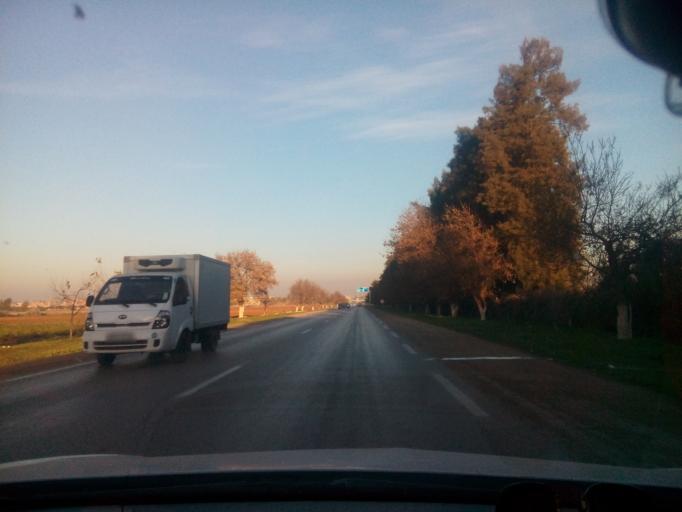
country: DZ
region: Chlef
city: Boukadir
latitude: 36.0540
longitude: 1.1008
